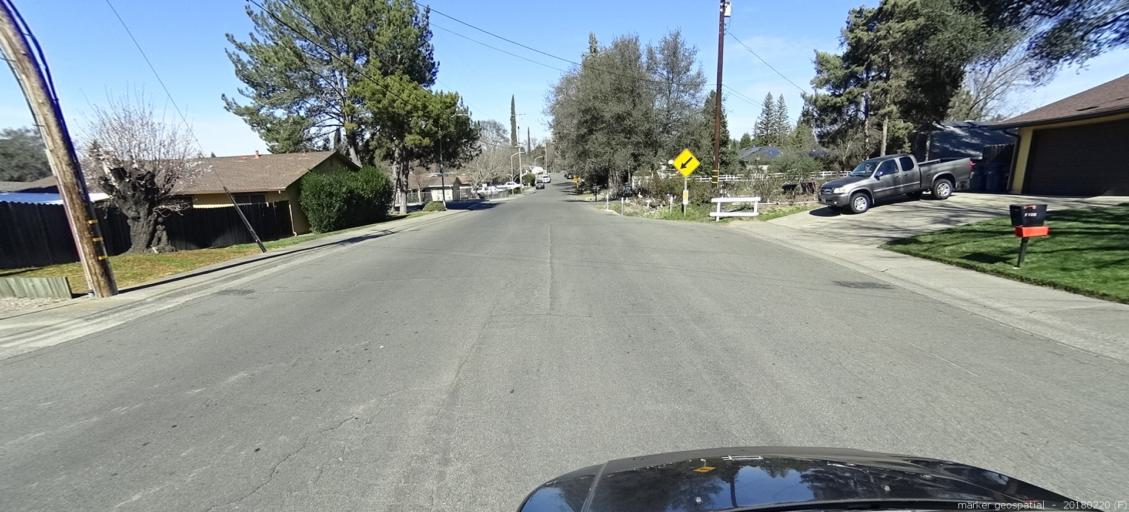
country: US
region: California
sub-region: Sacramento County
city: Orangevale
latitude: 38.7035
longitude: -121.2353
